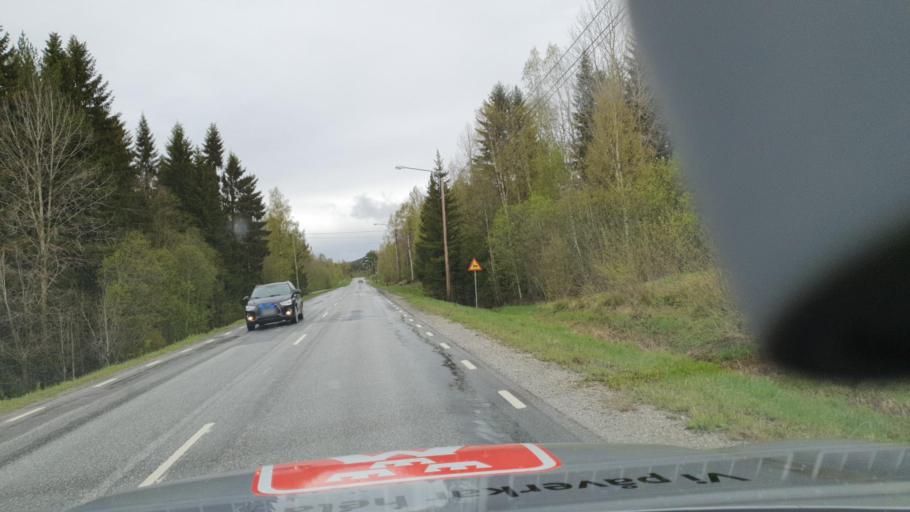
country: SE
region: Vaesternorrland
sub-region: OErnskoeldsviks Kommun
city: Bjasta
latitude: 63.3964
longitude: 18.4611
